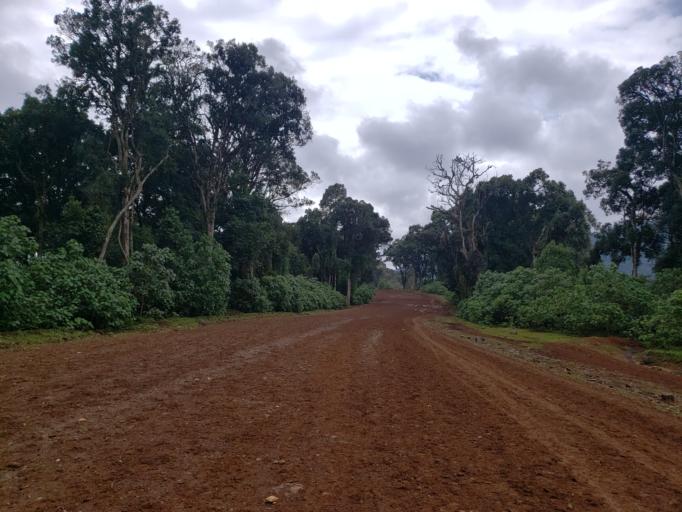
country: ET
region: Oromiya
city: Dodola
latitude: 6.6058
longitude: 39.4162
